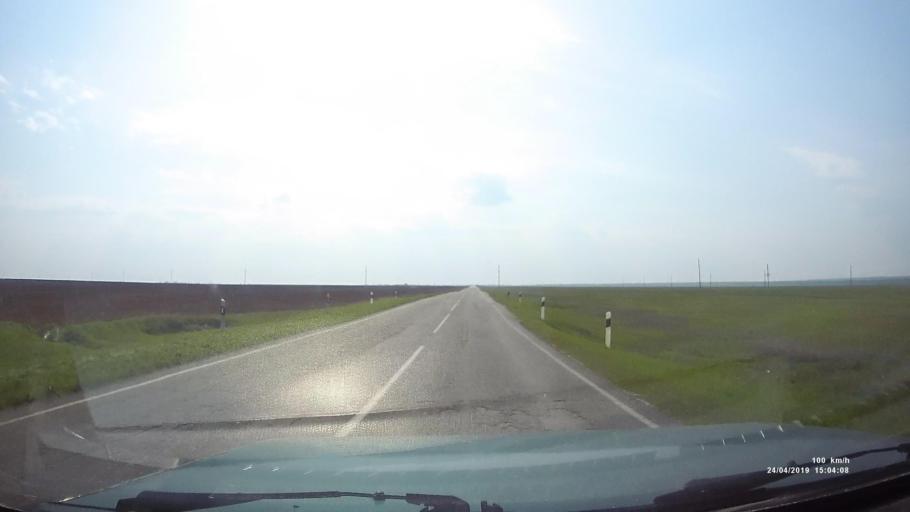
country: RU
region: Rostov
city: Remontnoye
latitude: 46.5631
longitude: 43.4771
